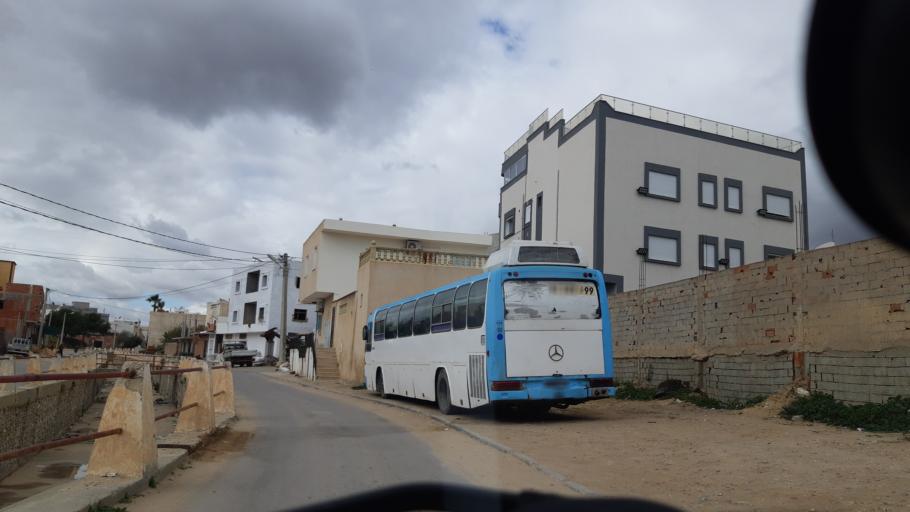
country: TN
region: Susah
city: Akouda
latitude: 35.8680
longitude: 10.5384
